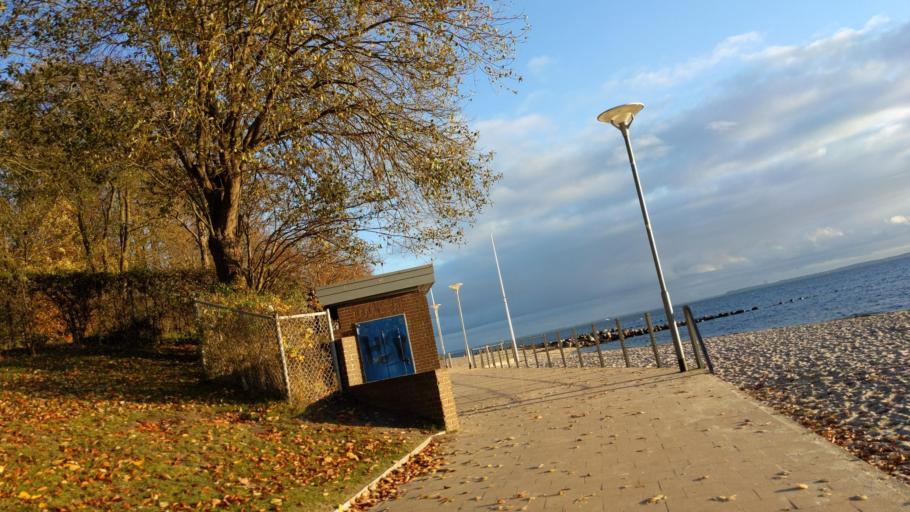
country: DE
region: Schleswig-Holstein
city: Neustadt in Holstein
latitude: 54.0931
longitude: 10.8152
